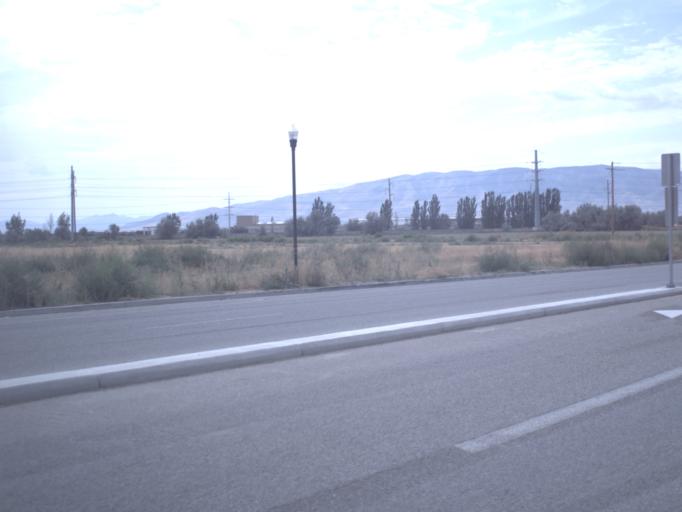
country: US
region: Utah
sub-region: Utah County
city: American Fork
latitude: 40.3477
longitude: -111.7730
